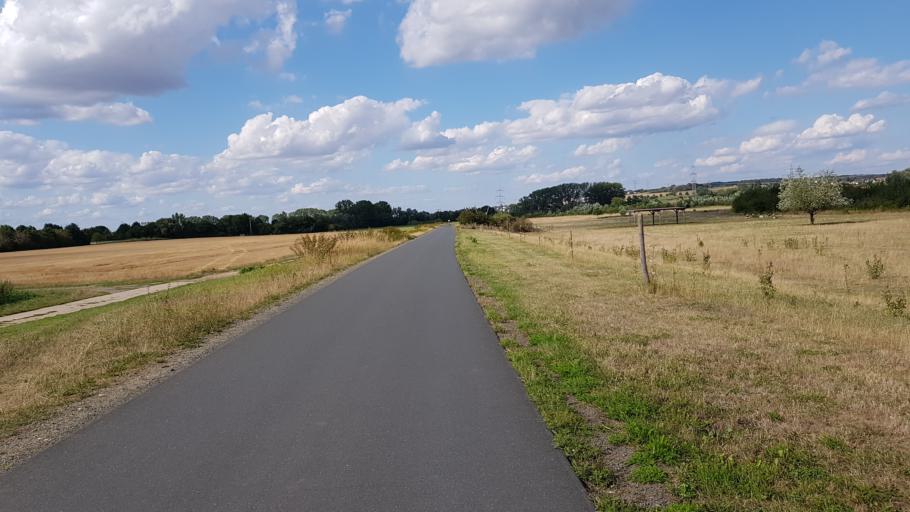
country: DE
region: Hesse
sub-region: Regierungsbezirk Darmstadt
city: Niederdorfelden
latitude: 50.2008
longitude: 8.7724
